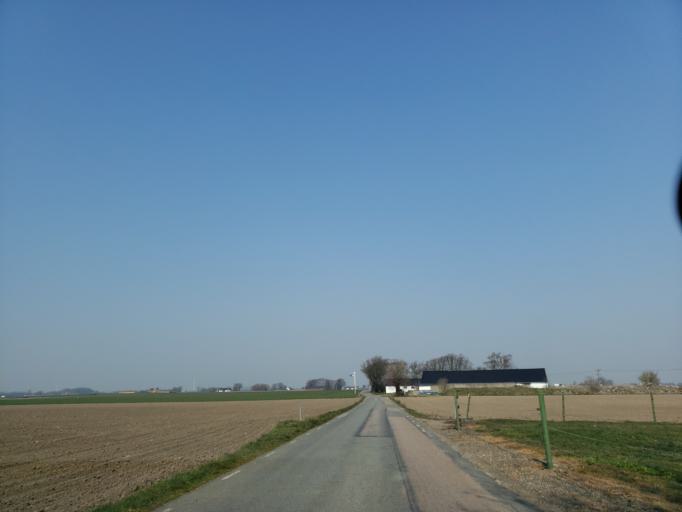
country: SE
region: Skane
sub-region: Simrishamns Kommun
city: Simrishamn
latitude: 55.4447
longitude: 14.2187
